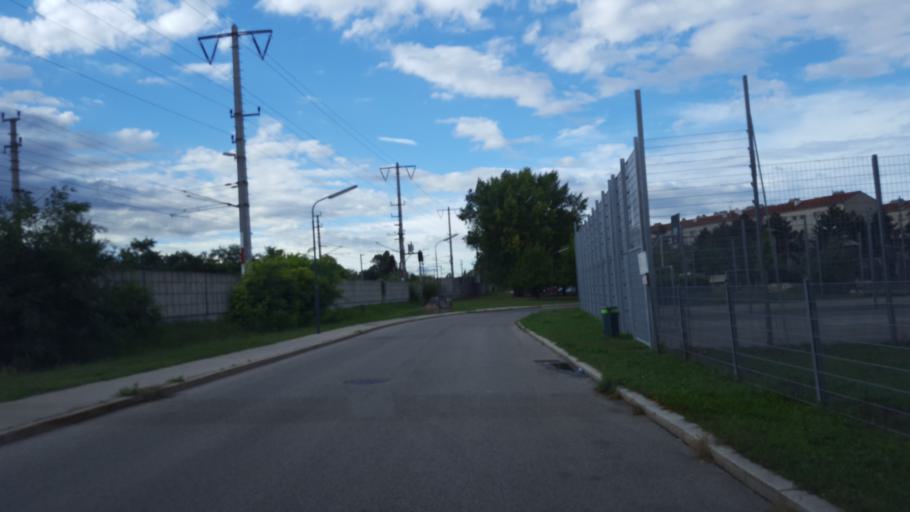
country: AT
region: Lower Austria
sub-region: Politischer Bezirk Wien-Umgebung
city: Schwechat
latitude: 48.1568
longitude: 16.4247
